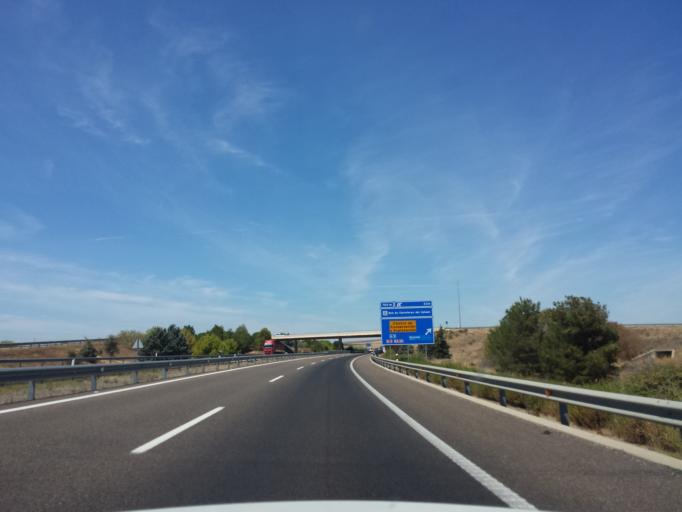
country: ES
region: Extremadura
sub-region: Provincia de Badajoz
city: Trujillanos
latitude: 38.9475
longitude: -6.2647
